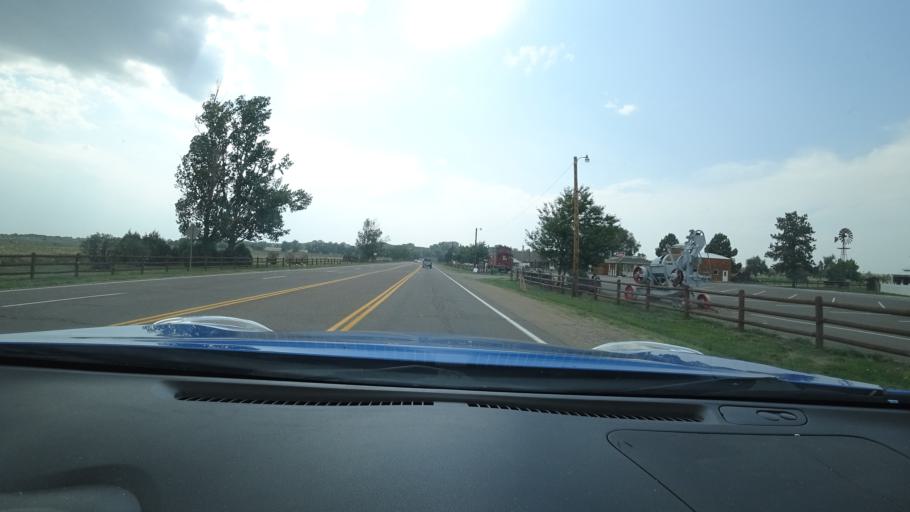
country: US
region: Colorado
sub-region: Adams County
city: Todd Creek
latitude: 39.9249
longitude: -104.8763
